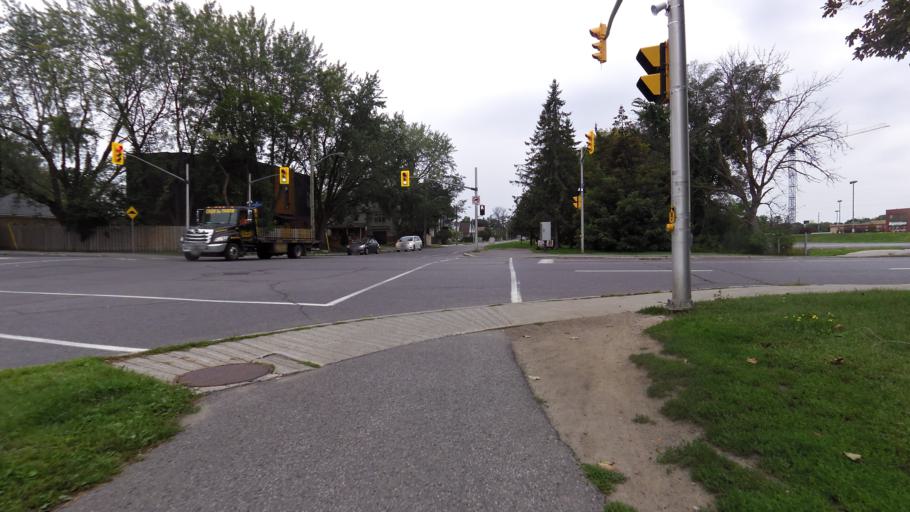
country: CA
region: Ontario
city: Ottawa
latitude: 45.3935
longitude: -75.7455
